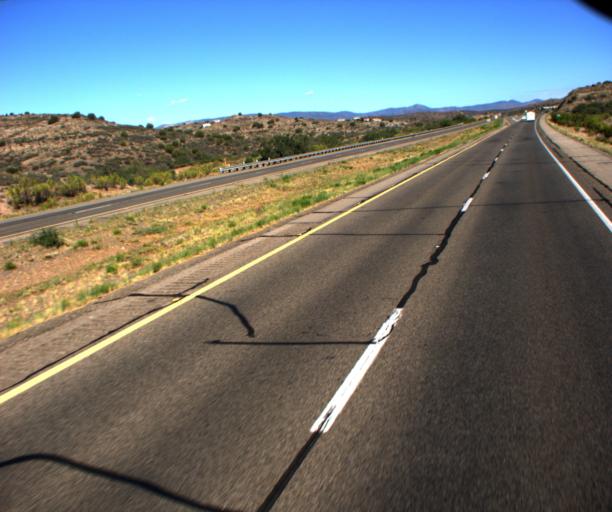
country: US
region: Arizona
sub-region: Yavapai County
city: Spring Valley
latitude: 34.3614
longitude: -112.1730
